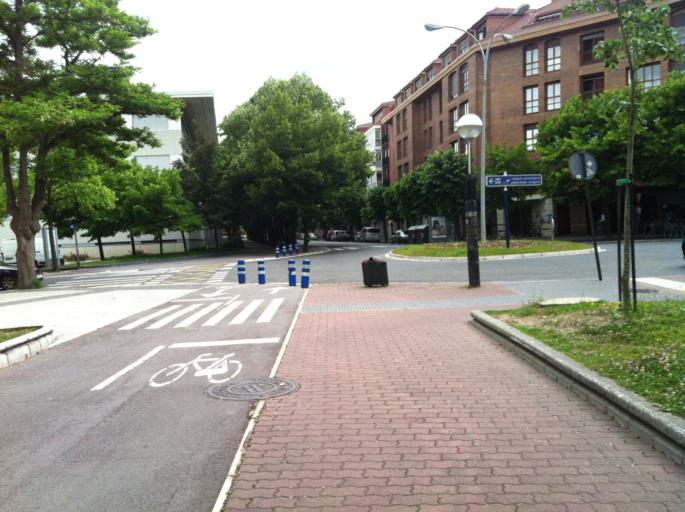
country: ES
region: Basque Country
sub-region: Provincia de Alava
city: Gasteiz / Vitoria
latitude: 42.8386
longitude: -2.6723
